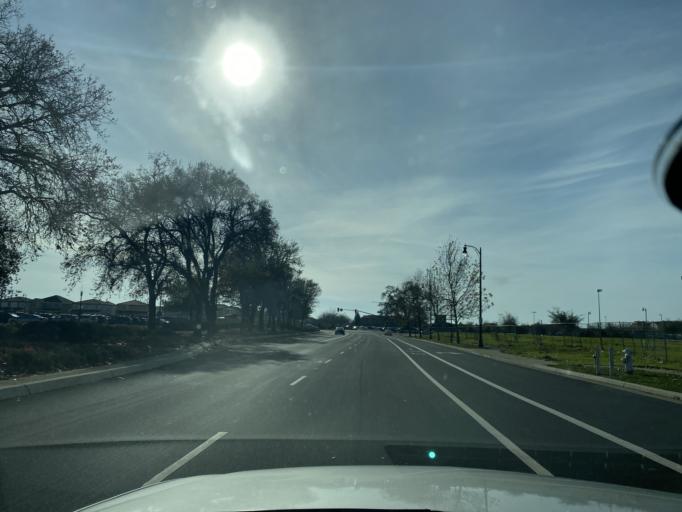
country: US
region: California
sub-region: Sacramento County
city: Elk Grove
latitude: 38.4029
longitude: -121.3949
